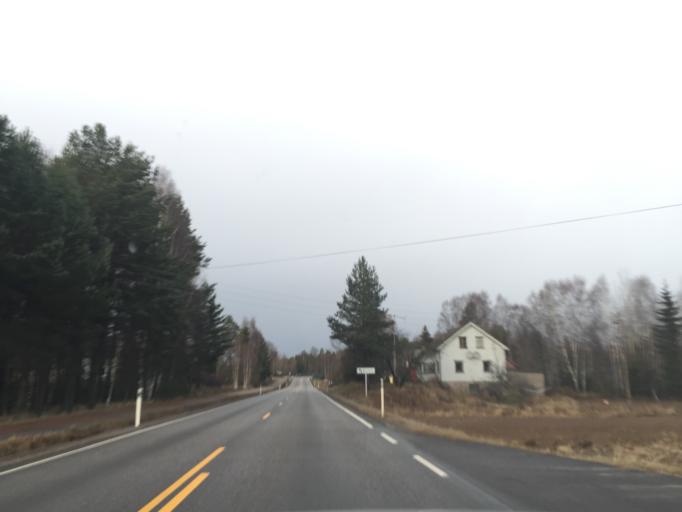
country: NO
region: Hedmark
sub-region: Asnes
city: Flisa
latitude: 60.5806
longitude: 12.0503
